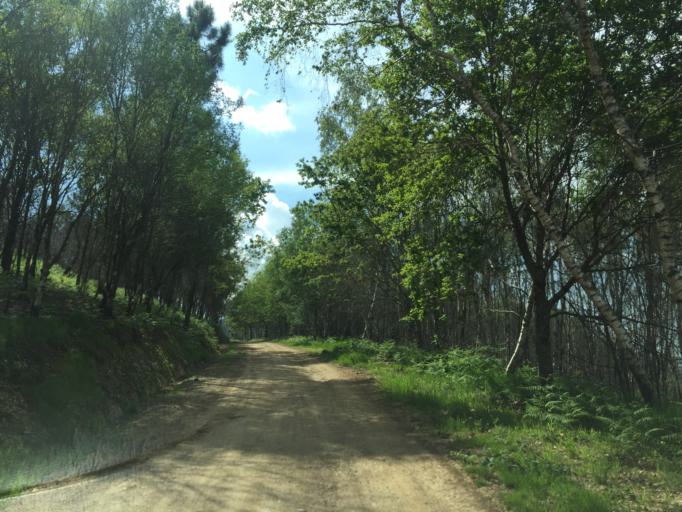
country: PT
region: Coimbra
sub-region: Arganil
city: Arganil
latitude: 40.1864
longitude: -7.9809
